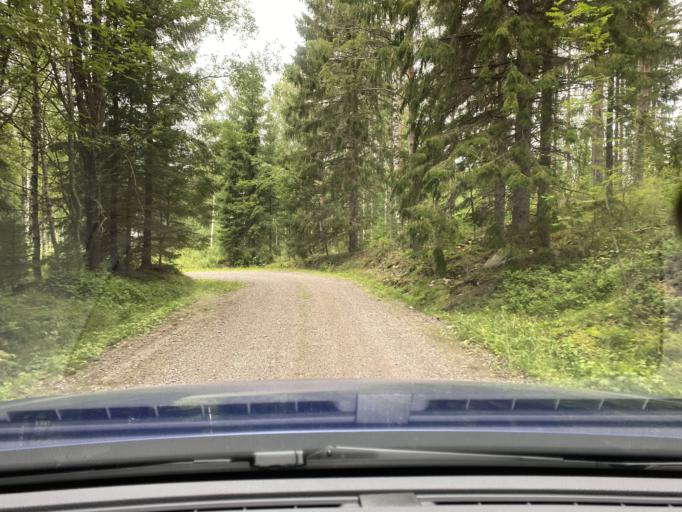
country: FI
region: Pirkanmaa
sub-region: Ylae-Pirkanmaa
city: Maenttae
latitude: 62.0190
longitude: 24.7567
